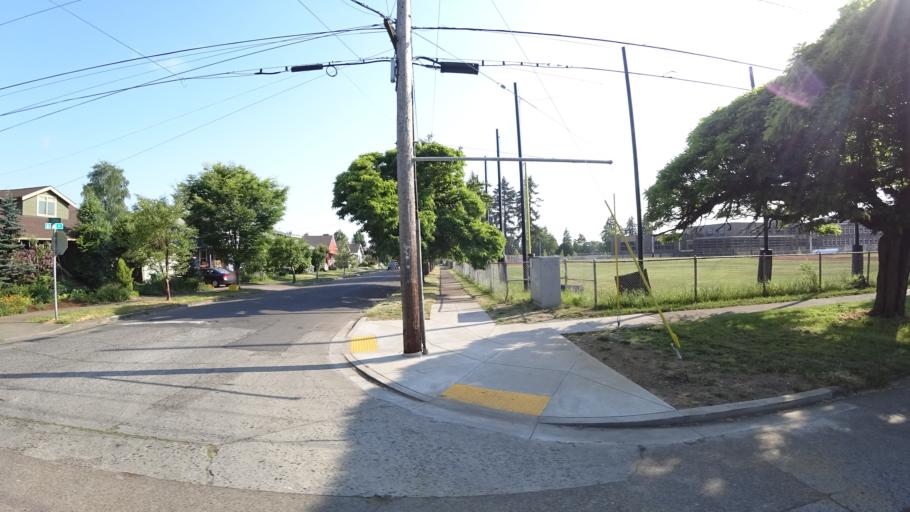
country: US
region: Oregon
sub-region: Washington County
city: West Haven
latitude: 45.5890
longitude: -122.7409
